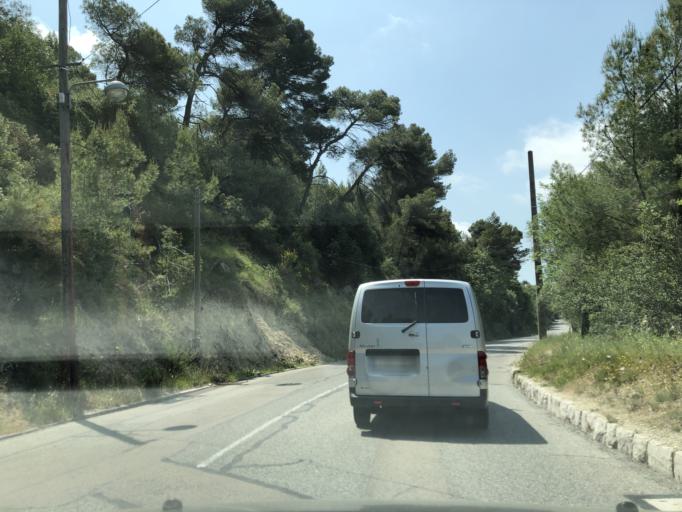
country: FR
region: Provence-Alpes-Cote d'Azur
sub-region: Departement des Alpes-Maritimes
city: Saint-Andre-de-la-Roche
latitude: 43.7300
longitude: 7.2958
